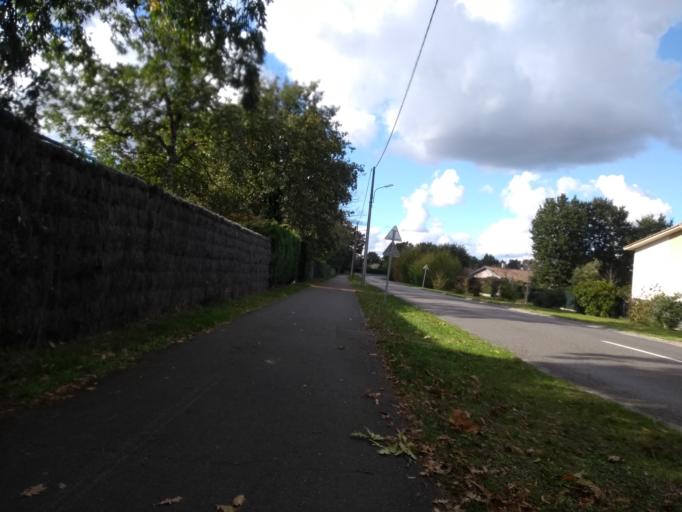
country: FR
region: Aquitaine
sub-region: Departement de la Gironde
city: Cestas
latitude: 44.7368
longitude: -0.6738
